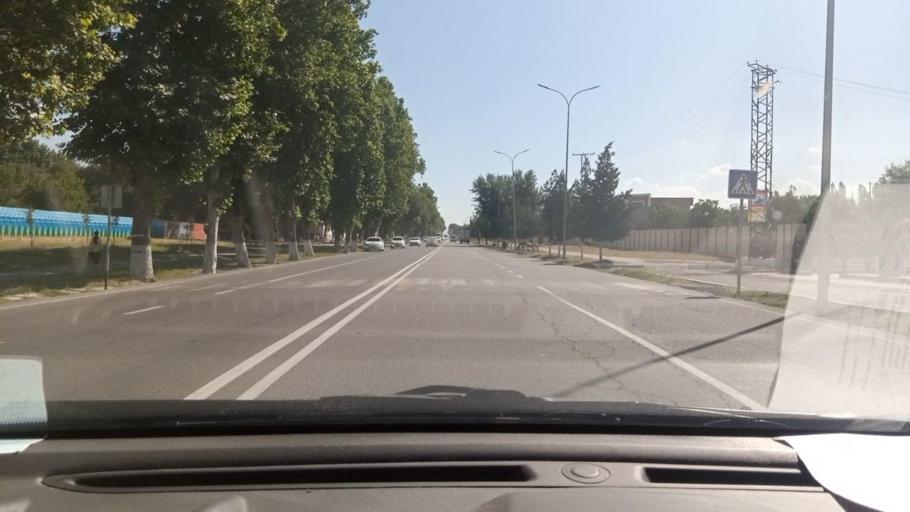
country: UZ
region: Toshkent
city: Angren
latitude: 40.9977
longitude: 70.0700
